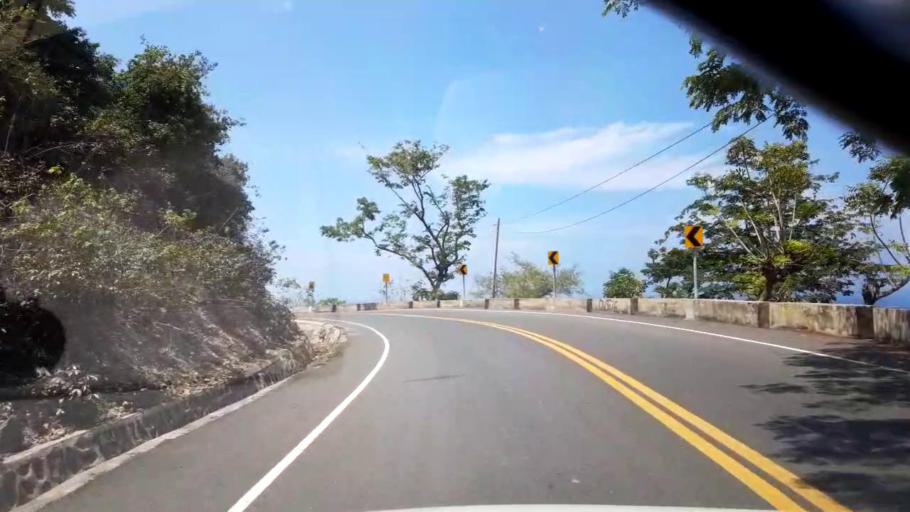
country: TL
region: Liquica
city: Maubara
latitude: -8.6588
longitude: 125.1153
